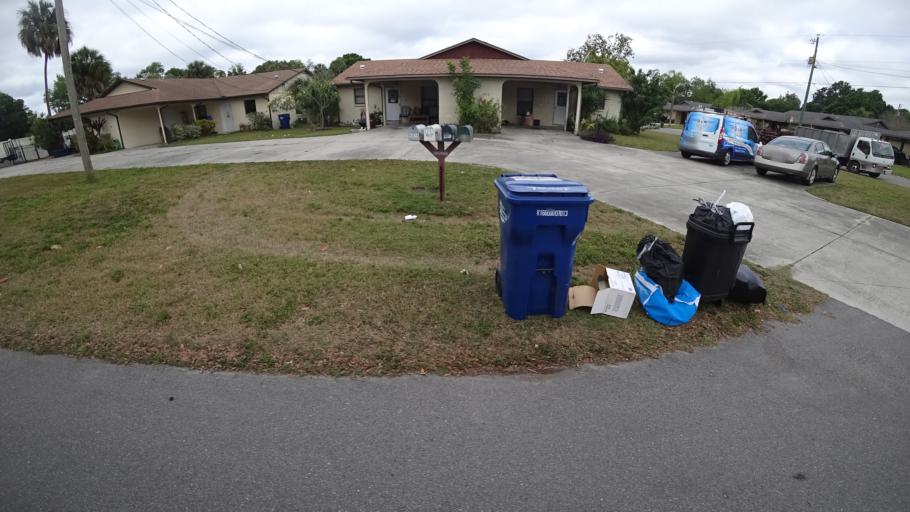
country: US
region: Florida
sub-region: Manatee County
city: South Bradenton
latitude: 27.4554
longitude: -82.5891
